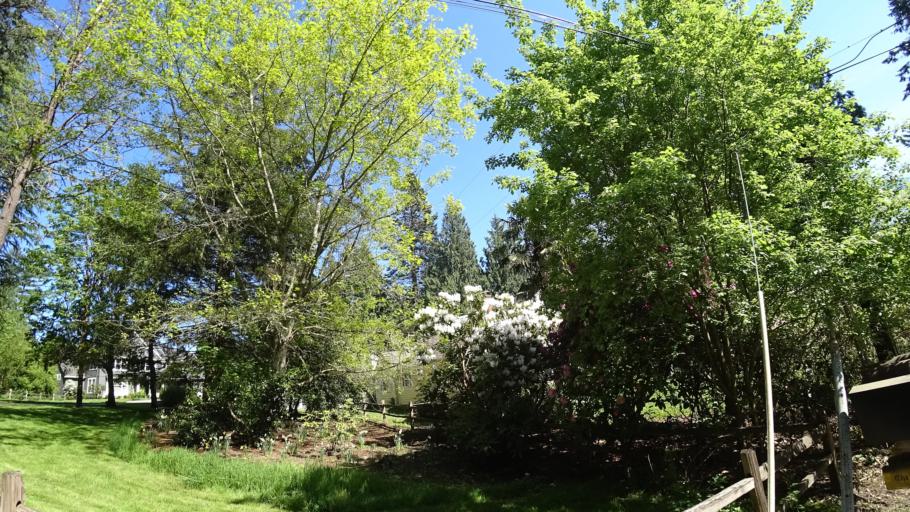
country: US
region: Oregon
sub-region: Washington County
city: West Slope
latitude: 45.4934
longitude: -122.7367
